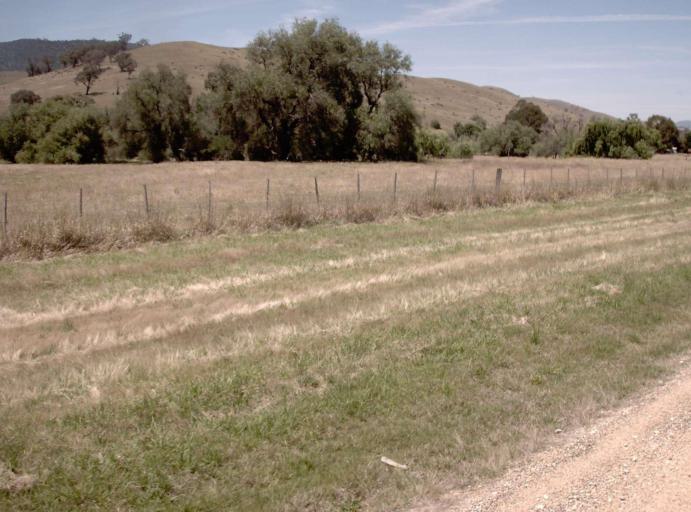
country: AU
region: Victoria
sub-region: East Gippsland
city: Bairnsdale
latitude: -37.1971
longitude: 147.7232
